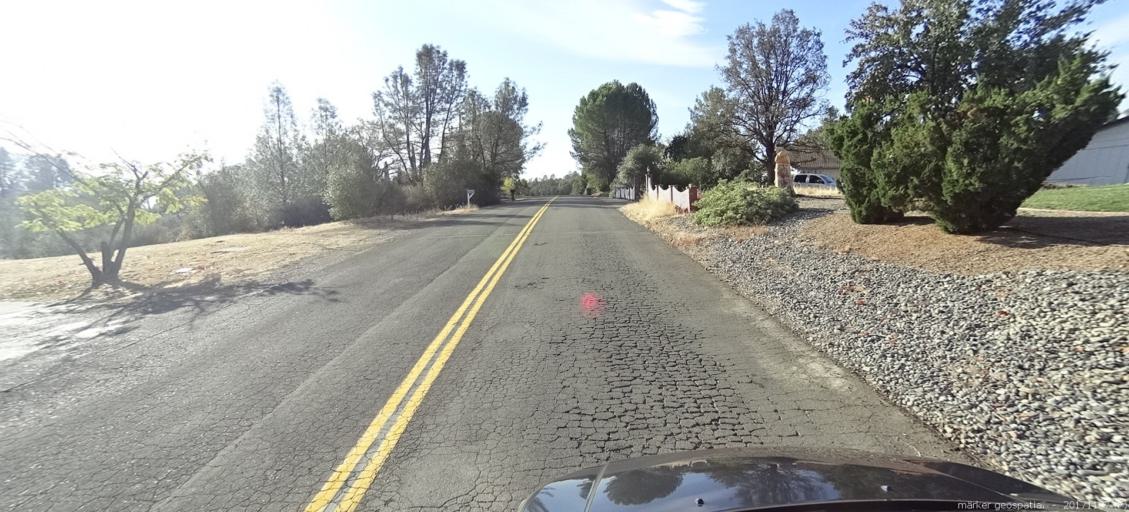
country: US
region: California
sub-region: Shasta County
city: Shasta
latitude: 40.5434
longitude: -122.4572
